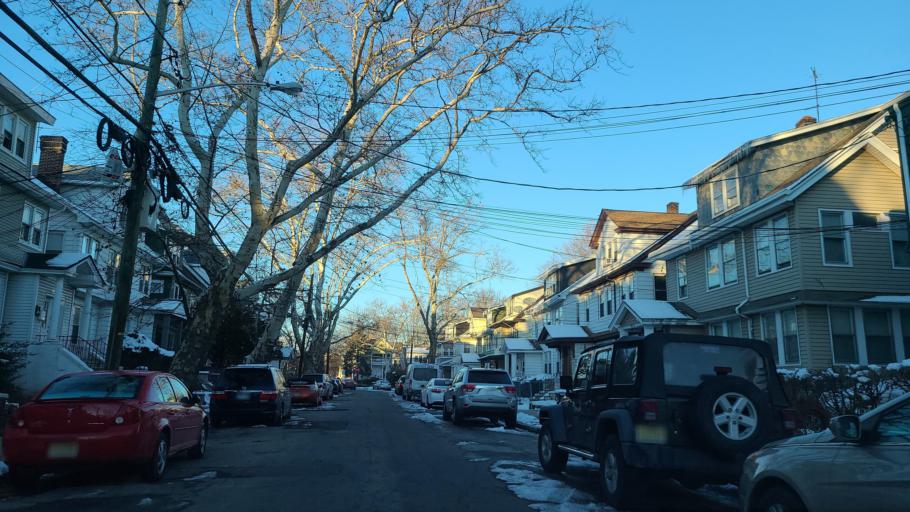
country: US
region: New Jersey
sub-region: Essex County
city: Irvington
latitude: 40.7475
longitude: -74.2341
